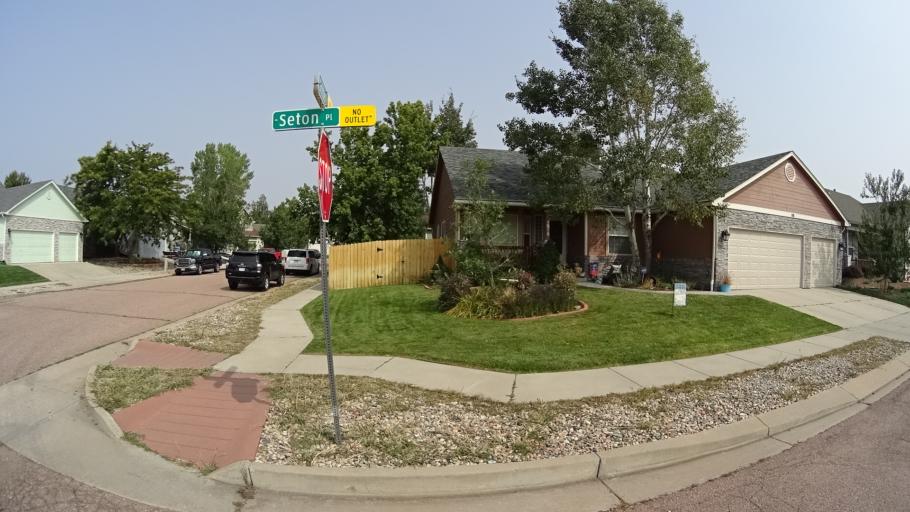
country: US
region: Colorado
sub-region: El Paso County
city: Cimarron Hills
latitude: 38.9175
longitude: -104.7375
